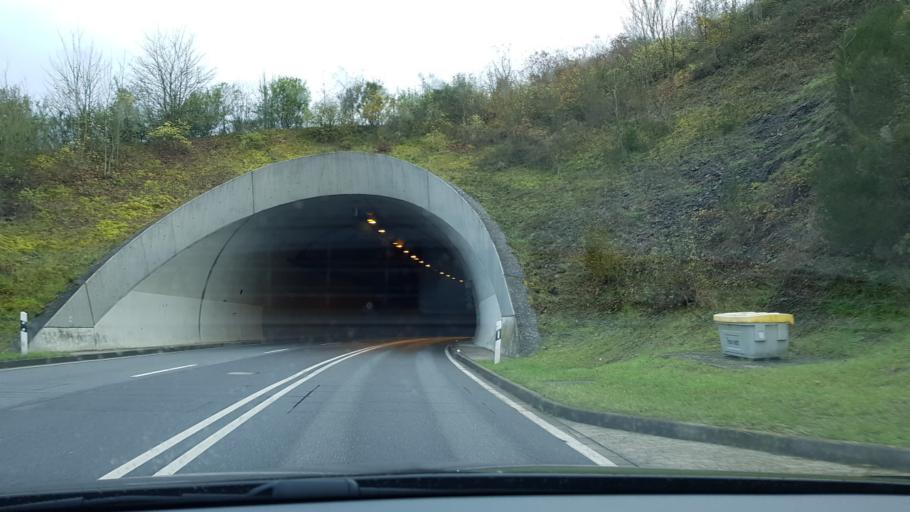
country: DE
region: Rheinland-Pfalz
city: Altenahr
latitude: 50.5198
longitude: 6.9871
